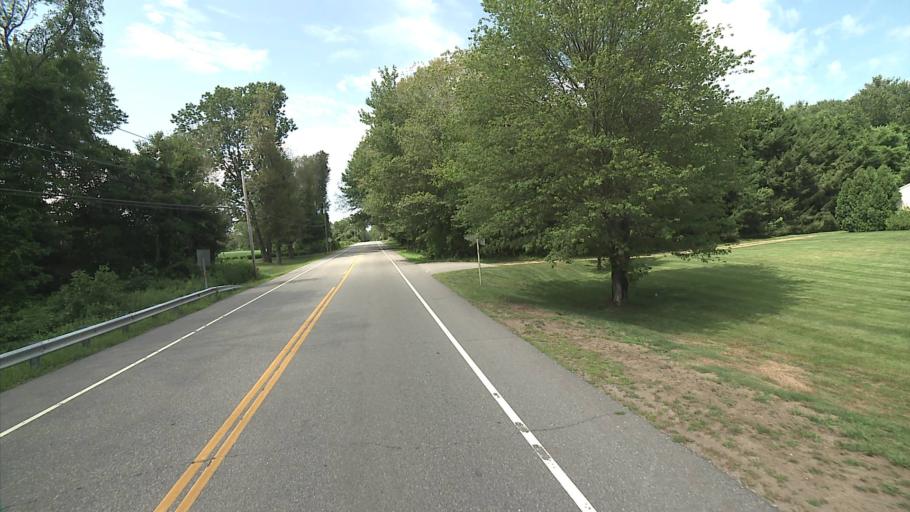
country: US
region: Connecticut
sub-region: New London County
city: Colchester
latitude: 41.5450
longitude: -72.2749
